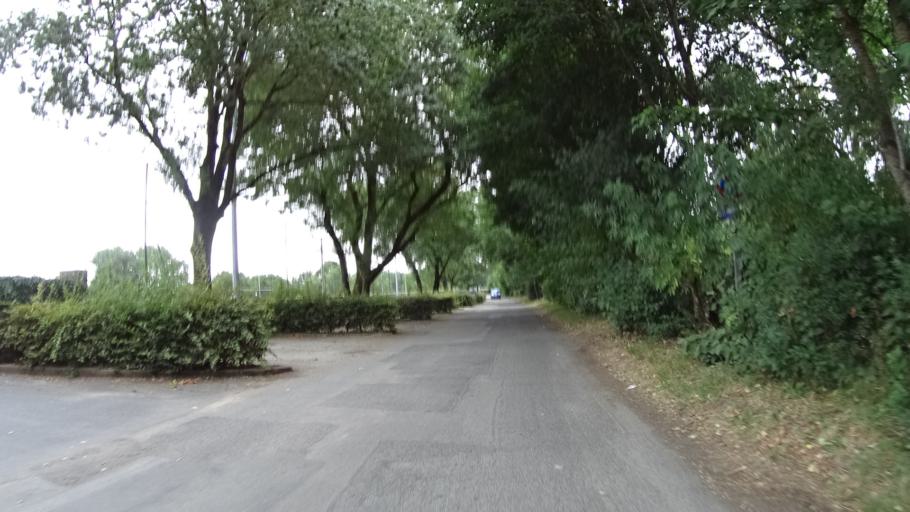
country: FR
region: Pays de la Loire
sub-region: Departement de la Loire-Atlantique
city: Sainte-Luce-sur-Loire
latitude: 47.2437
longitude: -1.4630
